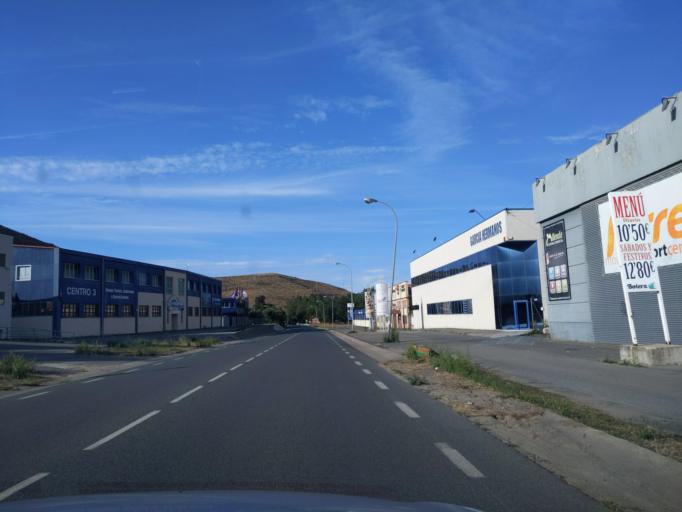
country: ES
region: La Rioja
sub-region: Provincia de La Rioja
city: Ezcaray
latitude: 42.3342
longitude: -3.0118
